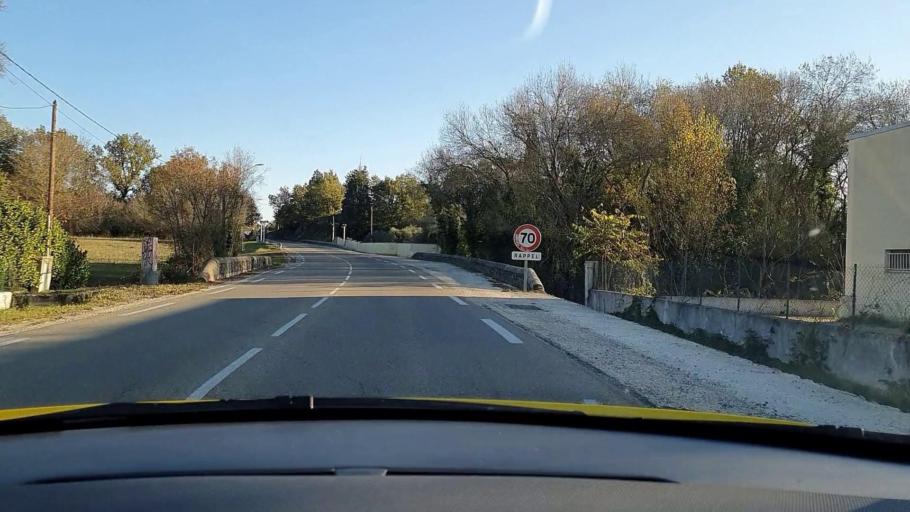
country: FR
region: Languedoc-Roussillon
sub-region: Departement du Gard
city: Salindres
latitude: 44.1707
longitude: 4.1404
